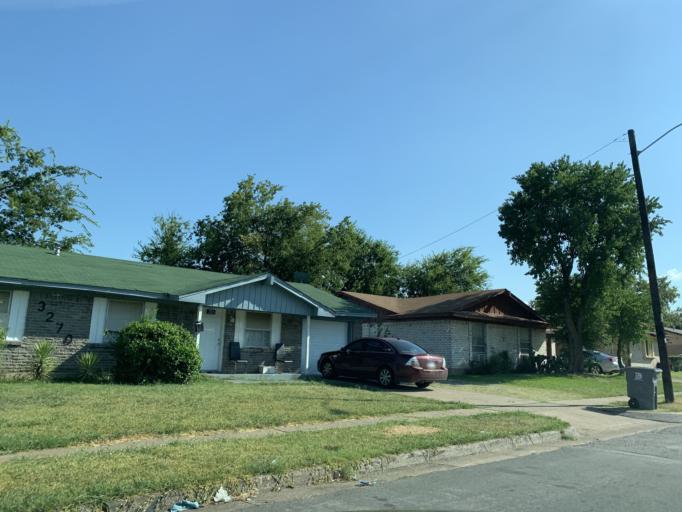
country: US
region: Texas
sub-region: Dallas County
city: Hutchins
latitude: 32.6585
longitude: -96.7674
